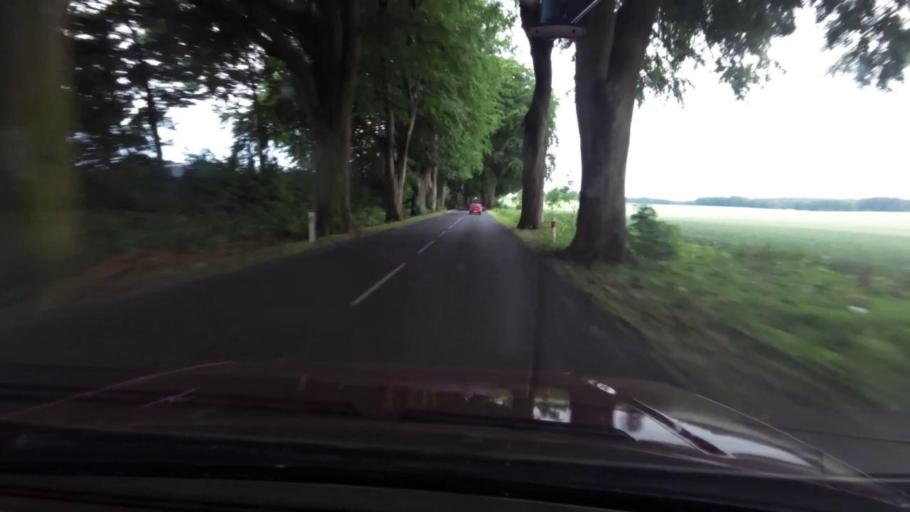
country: PL
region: West Pomeranian Voivodeship
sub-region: Powiat koszalinski
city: Polanow
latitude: 54.1400
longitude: 16.5554
